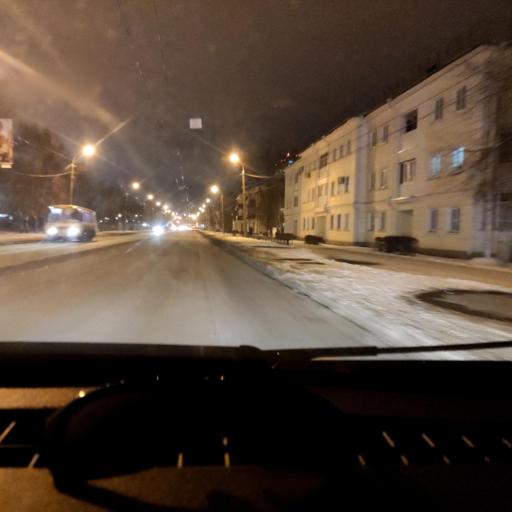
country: RU
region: Bashkortostan
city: Ufa
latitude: 54.7929
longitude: 56.1389
